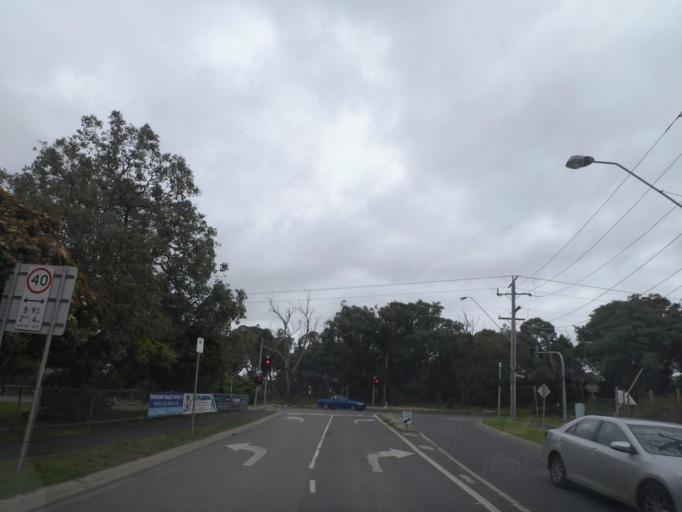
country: AU
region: Victoria
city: Plenty
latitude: -37.6395
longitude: 145.1328
